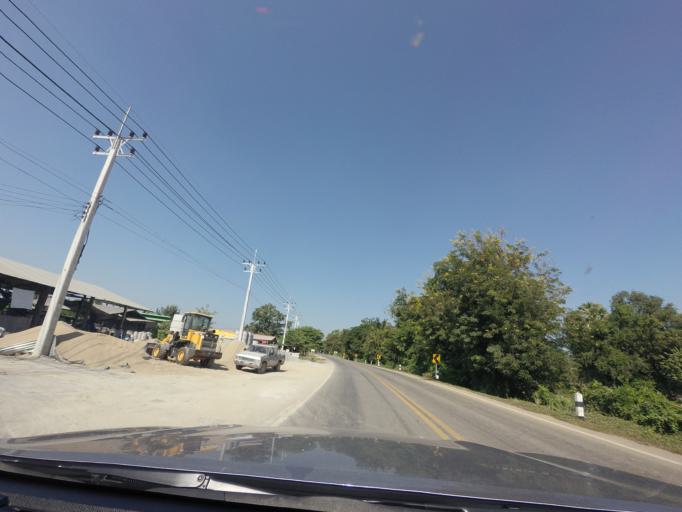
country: TH
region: Sukhothai
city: Sawankhalok
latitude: 17.3345
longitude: 99.8267
